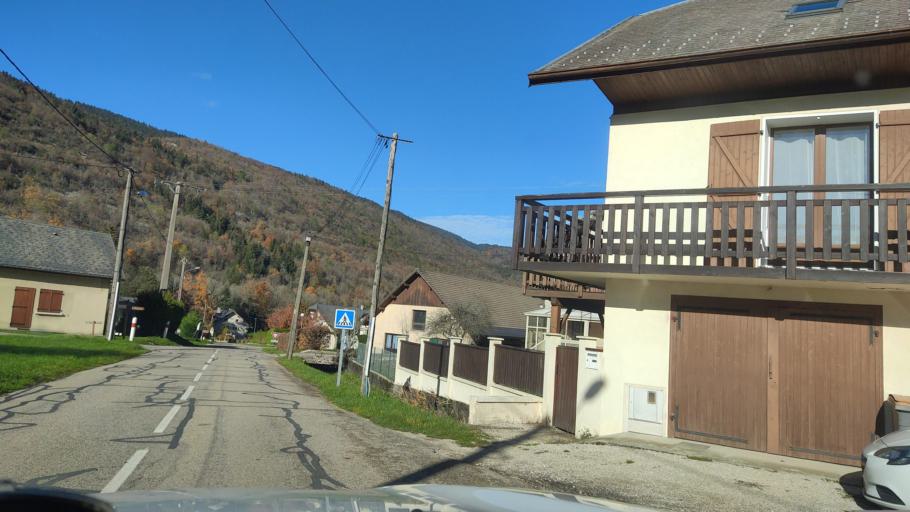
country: FR
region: Rhone-Alpes
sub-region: Departement de la Savoie
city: Les Echelles
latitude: 45.4675
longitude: 5.8188
